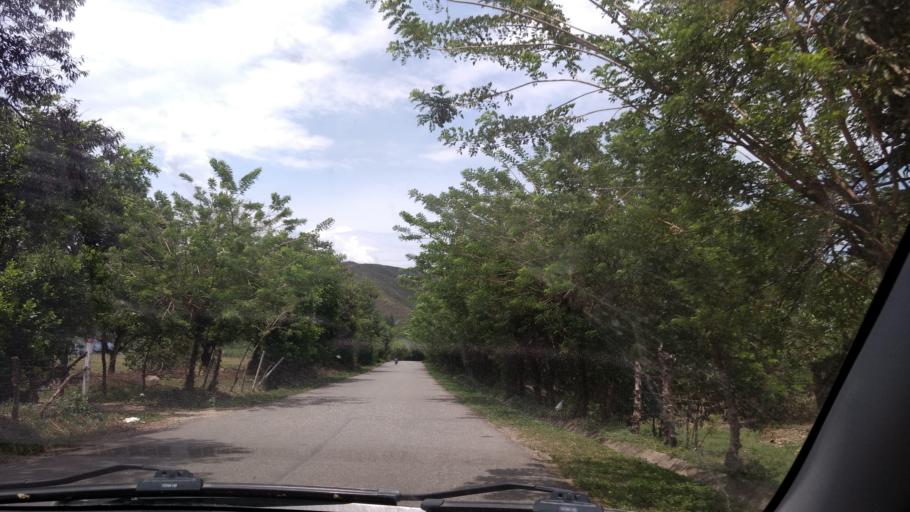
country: CO
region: Cauca
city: Buenos Aires
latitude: 3.0691
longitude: -76.6545
